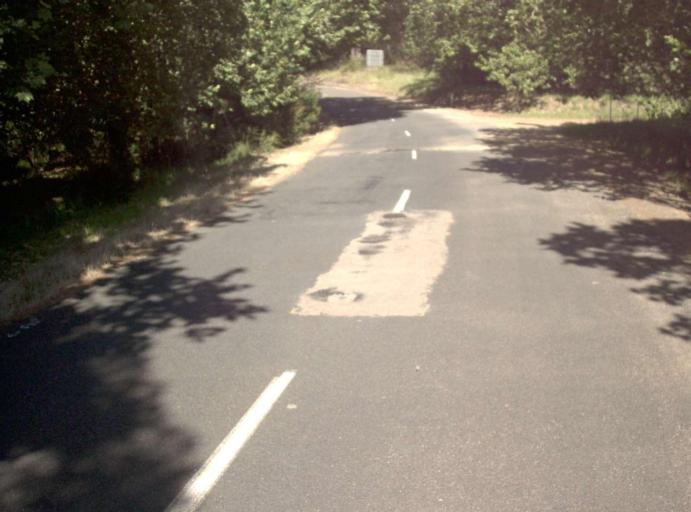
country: AU
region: Victoria
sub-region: East Gippsland
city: Lakes Entrance
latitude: -37.5041
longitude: 148.5374
